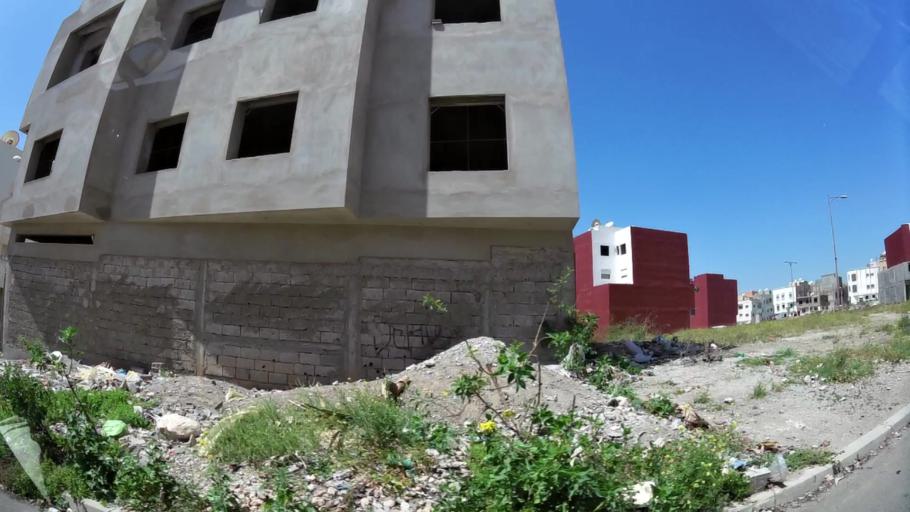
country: MA
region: Oued ed Dahab-Lagouira
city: Dakhla
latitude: 30.4359
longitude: -9.5481
